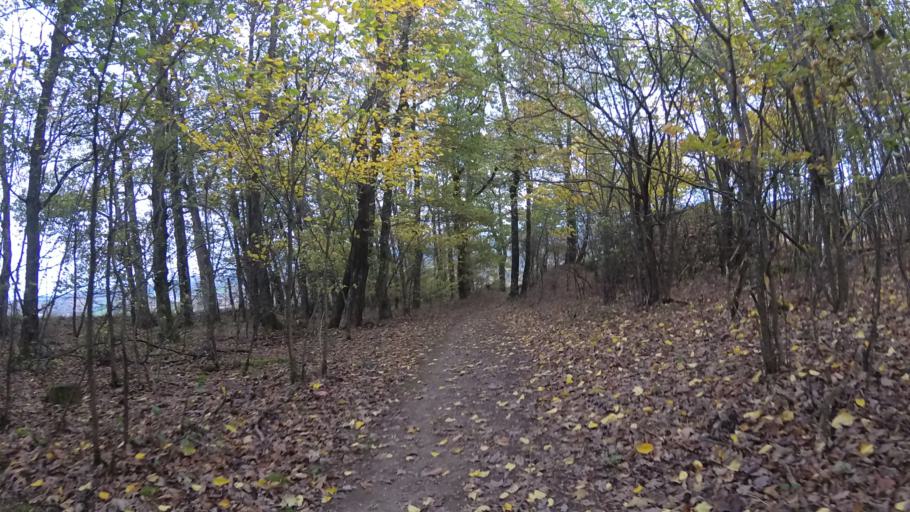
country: DE
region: Saarland
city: Sankt Wendel
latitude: 49.4587
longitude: 7.1947
